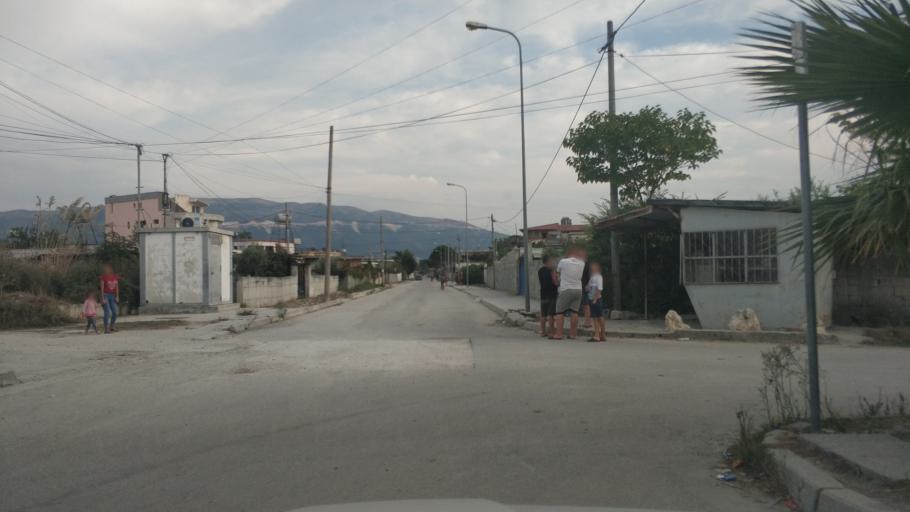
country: AL
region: Vlore
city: Vlore
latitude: 40.4663
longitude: 19.4654
